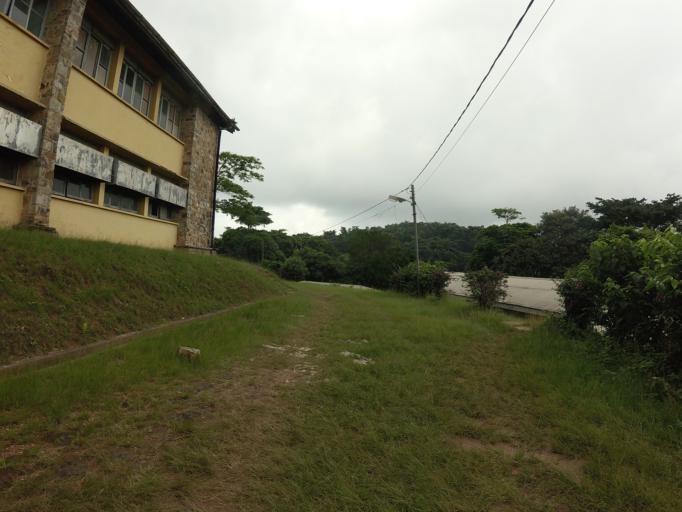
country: TG
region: Plateaux
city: Kpalime
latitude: 6.8421
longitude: 0.4370
